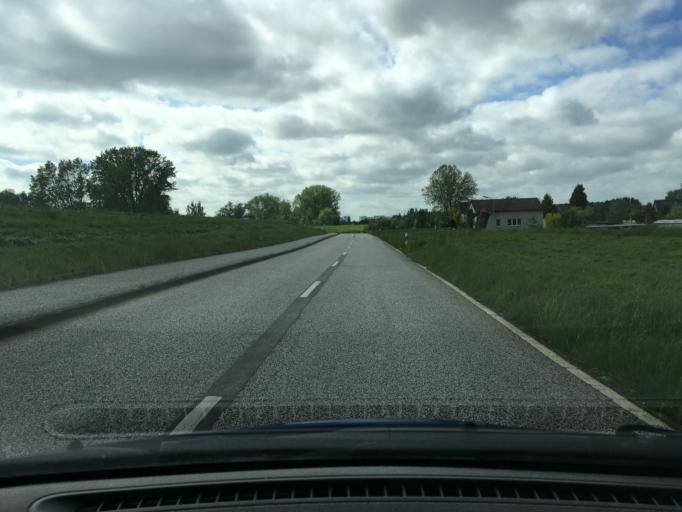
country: DE
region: Hamburg
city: Harburg
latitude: 53.4744
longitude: 10.0426
